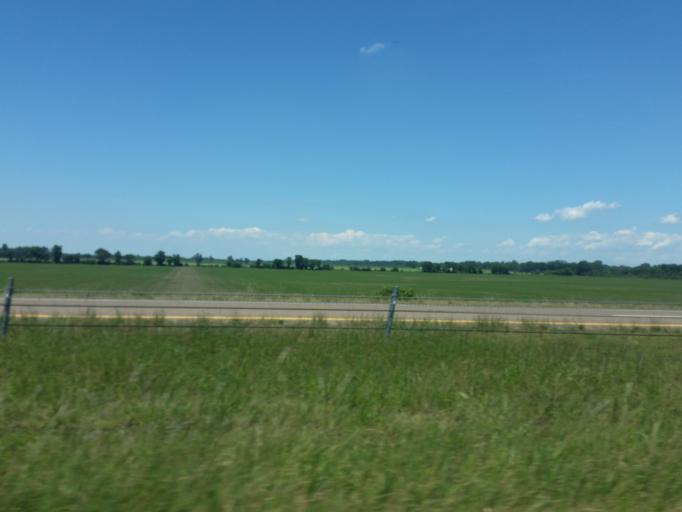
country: US
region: Missouri
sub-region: Pemiscot County
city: Caruthersville
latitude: 36.0945
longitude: -89.5928
